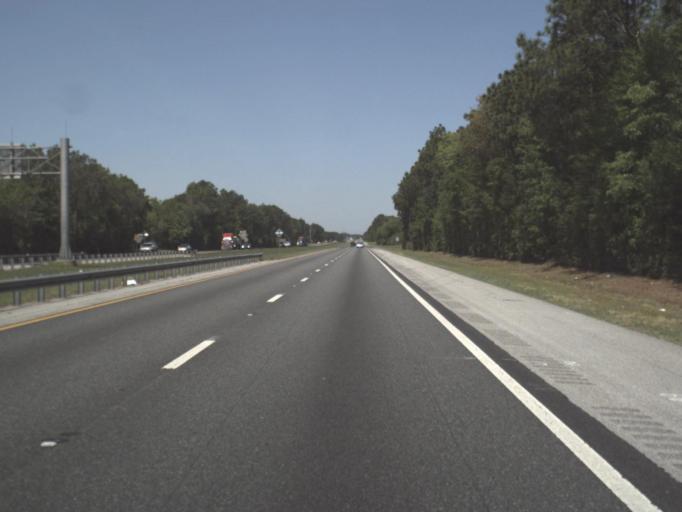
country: US
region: Florida
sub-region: Escambia County
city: Ensley
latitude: 30.5077
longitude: -87.2875
